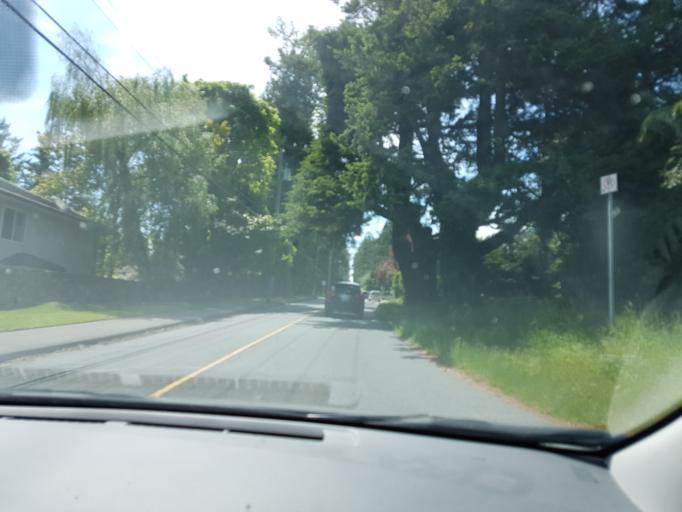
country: CA
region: British Columbia
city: Oak Bay
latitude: 48.4811
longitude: -123.3051
